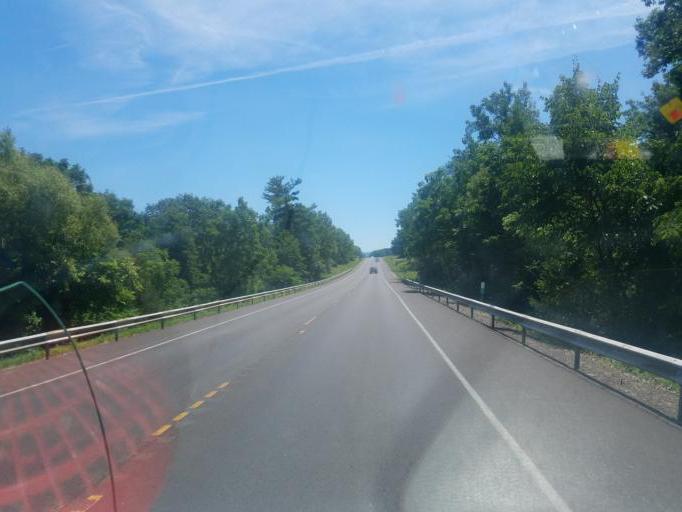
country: US
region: New York
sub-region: Yates County
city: Dundee
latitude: 42.5824
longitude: -76.9339
